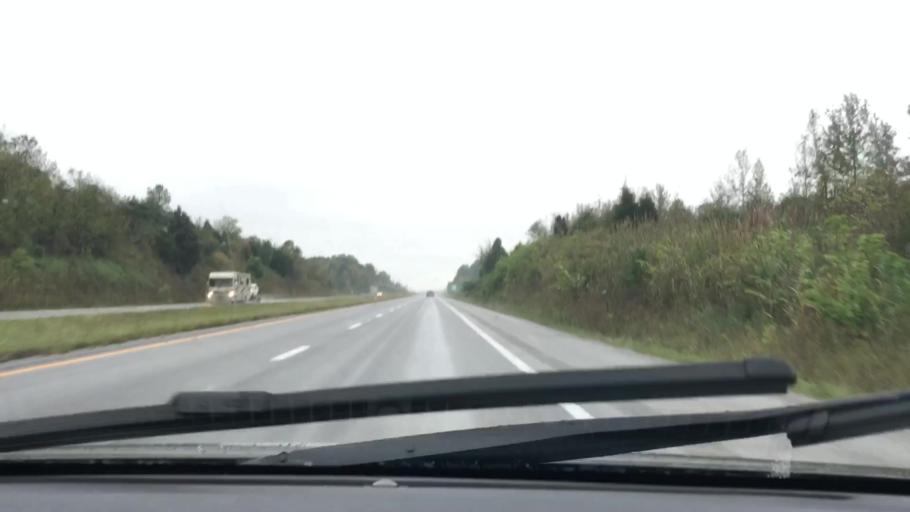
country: US
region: Kentucky
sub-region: Hopkins County
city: Nortonville
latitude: 37.1829
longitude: -87.4453
